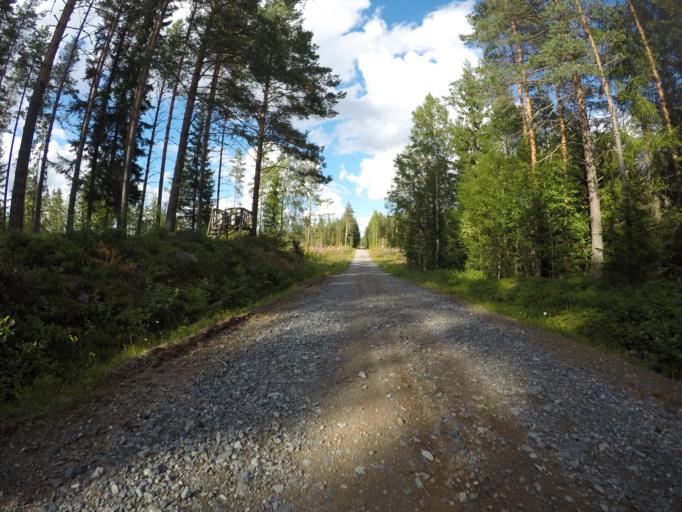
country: SE
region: OErebro
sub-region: Hallefors Kommun
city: Haellefors
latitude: 59.9204
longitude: 14.5593
